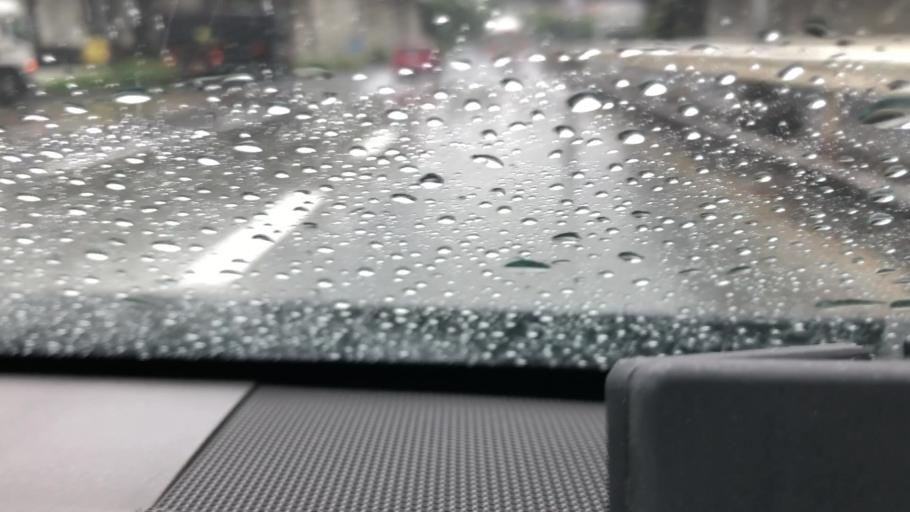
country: JP
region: Kanagawa
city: Yokohama
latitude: 35.4427
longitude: 139.5887
